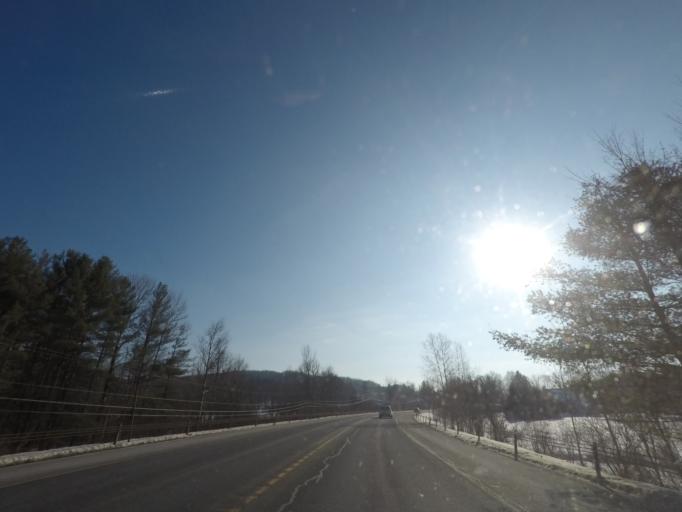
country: US
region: Massachusetts
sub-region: Berkshire County
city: Lanesborough
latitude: 42.5197
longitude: -73.3588
